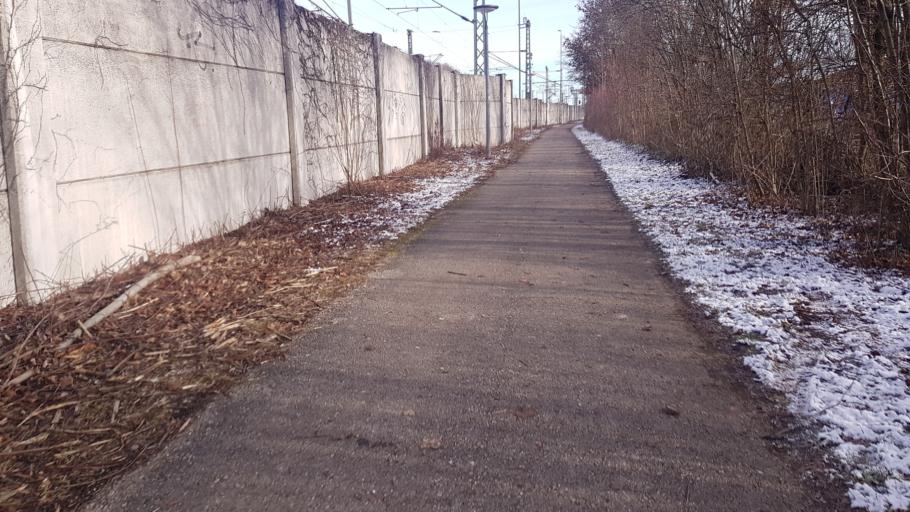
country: DE
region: Bavaria
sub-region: Upper Bavaria
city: Aschheim
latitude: 48.1450
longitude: 11.6871
